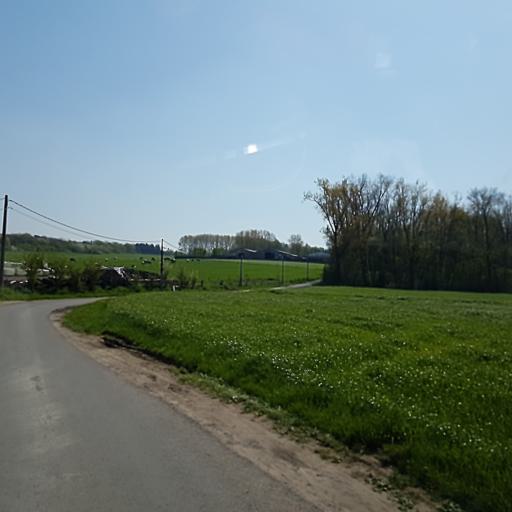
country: BE
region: Flanders
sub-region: Provincie West-Vlaanderen
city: Zonnebeke
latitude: 50.8542
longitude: 2.9698
